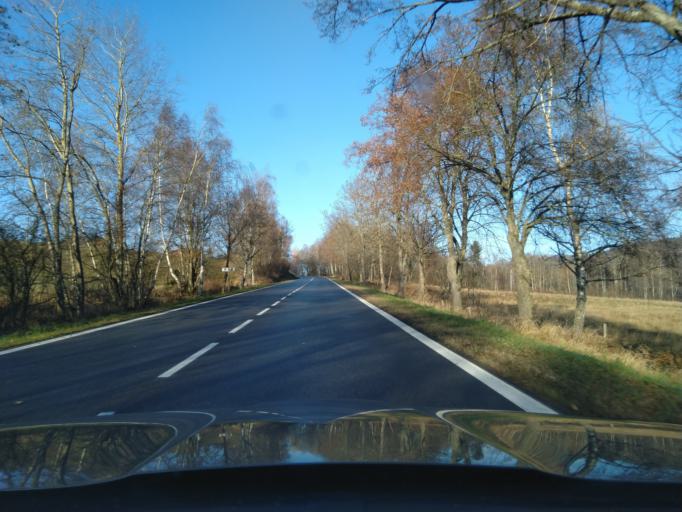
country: CZ
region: Jihocesky
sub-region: Okres Prachatice
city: Vimperk
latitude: 49.0626
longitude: 13.7533
